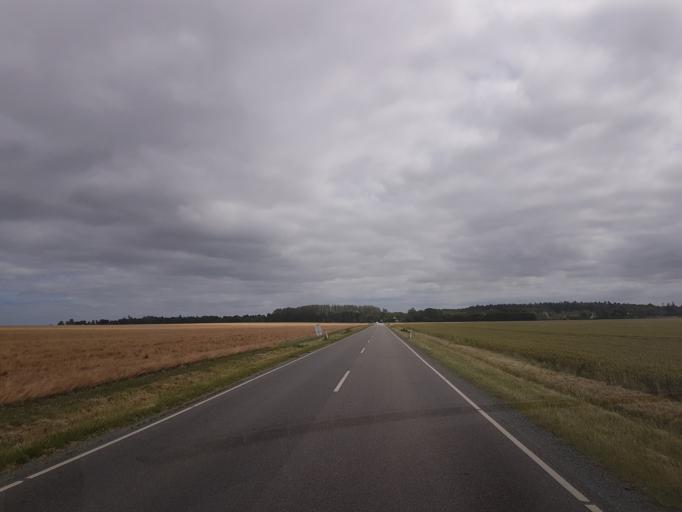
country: DK
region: South Denmark
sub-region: Nordfyns Kommune
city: Bogense
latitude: 55.5680
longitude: 10.1781
